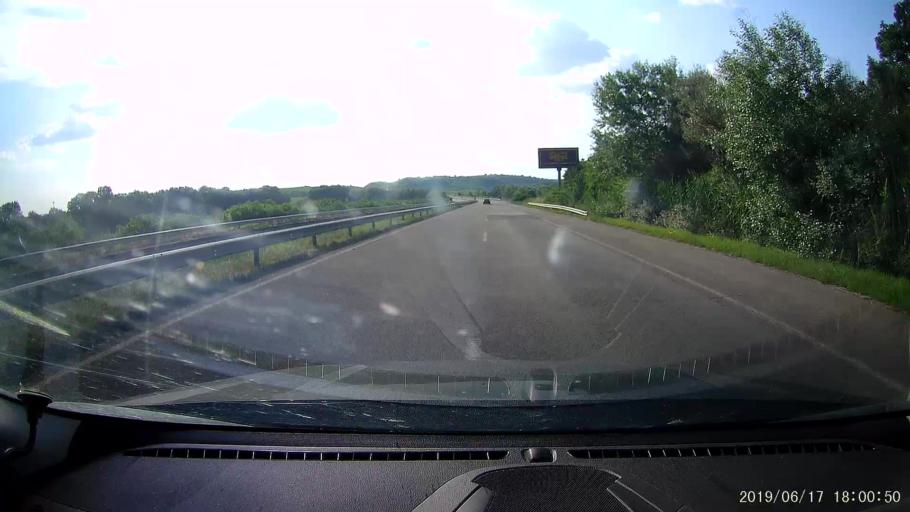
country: BG
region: Khaskovo
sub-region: Obshtina Svilengrad
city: Svilengrad
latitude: 41.7410
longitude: 26.2710
